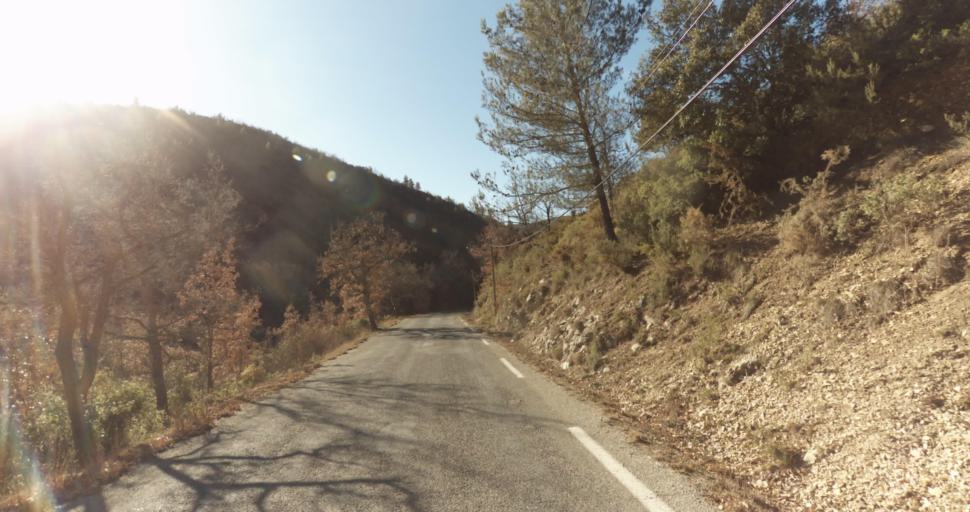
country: FR
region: Provence-Alpes-Cote d'Azur
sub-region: Departement des Bouches-du-Rhone
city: Peypin
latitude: 43.3755
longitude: 5.5657
